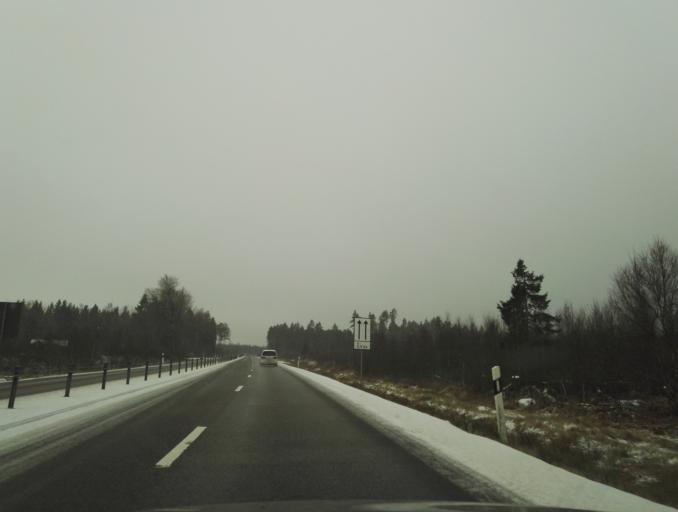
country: SE
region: Kronoberg
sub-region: Alvesta Kommun
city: Vislanda
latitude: 56.7609
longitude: 14.5238
